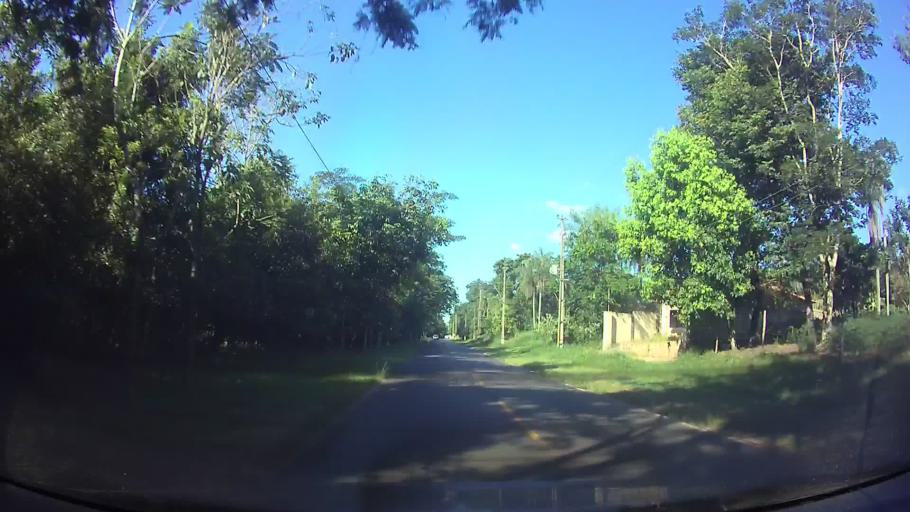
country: PY
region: Cordillera
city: Atyra
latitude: -25.2927
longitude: -57.1827
